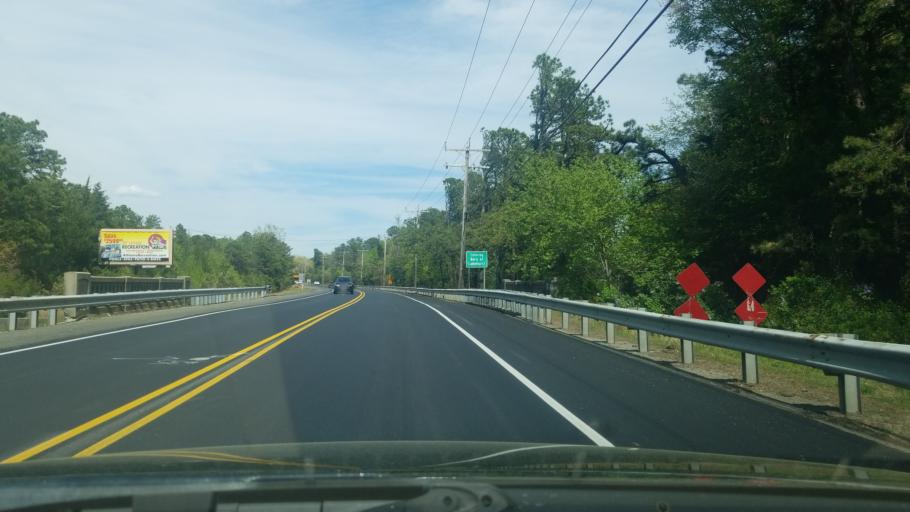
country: US
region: New Jersey
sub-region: Ocean County
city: Lakehurst
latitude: 40.0083
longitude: -74.3302
